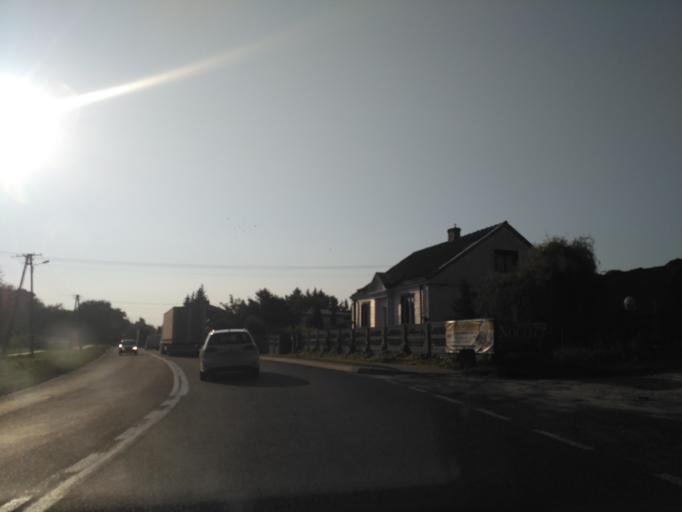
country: PL
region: Lublin Voivodeship
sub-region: Powiat janowski
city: Modliborzyce
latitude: 50.7573
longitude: 22.3225
